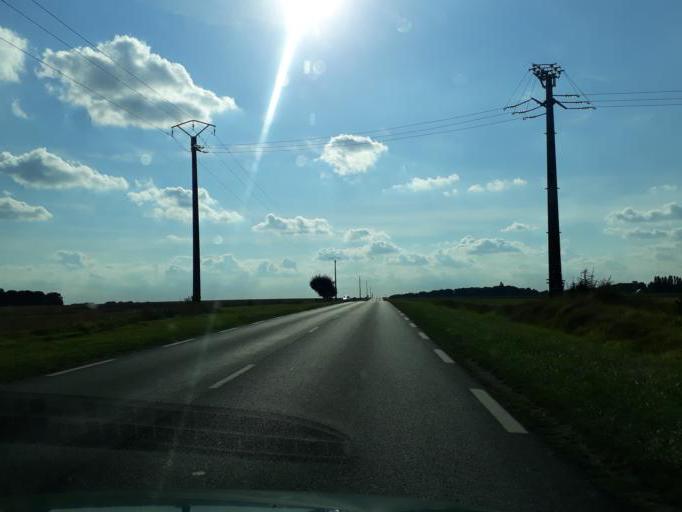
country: FR
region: Centre
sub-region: Departement du Loir-et-Cher
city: Oucques
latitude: 47.9043
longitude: 1.3483
